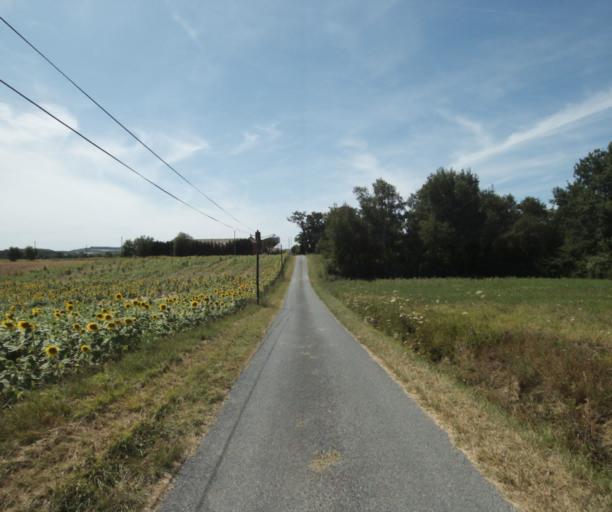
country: FR
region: Midi-Pyrenees
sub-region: Departement du Tarn
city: Puylaurens
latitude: 43.5352
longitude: 2.0014
